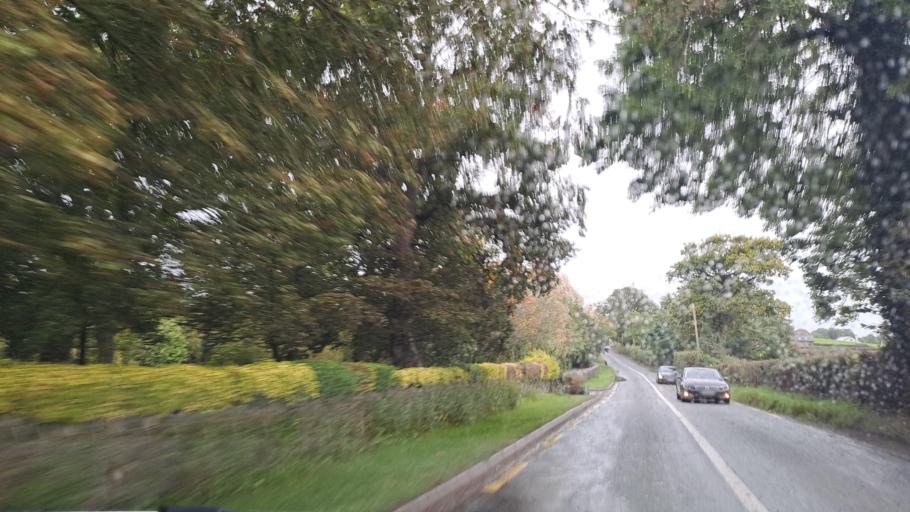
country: IE
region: Leinster
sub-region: Lu
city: Dundalk
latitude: 53.9627
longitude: -6.4594
